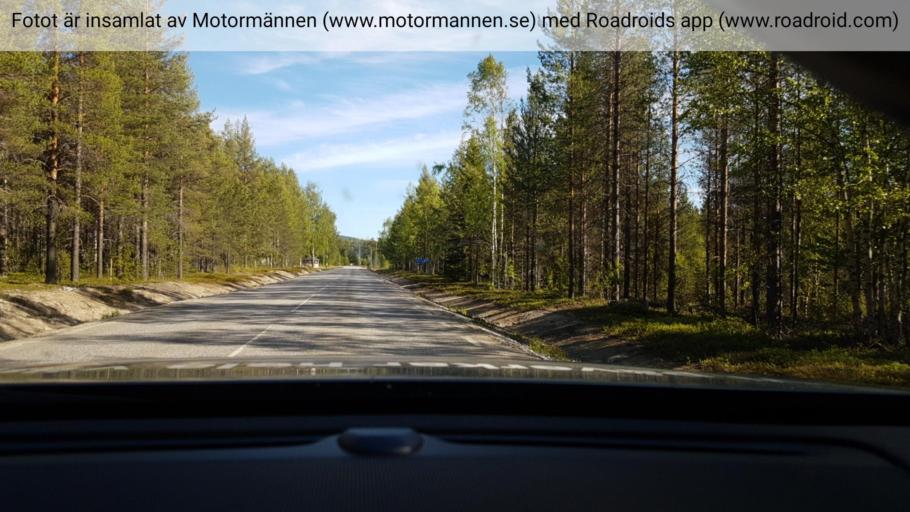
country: SE
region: Vaesterbotten
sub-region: Norsjo Kommun
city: Norsjoe
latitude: 64.7065
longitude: 19.1553
